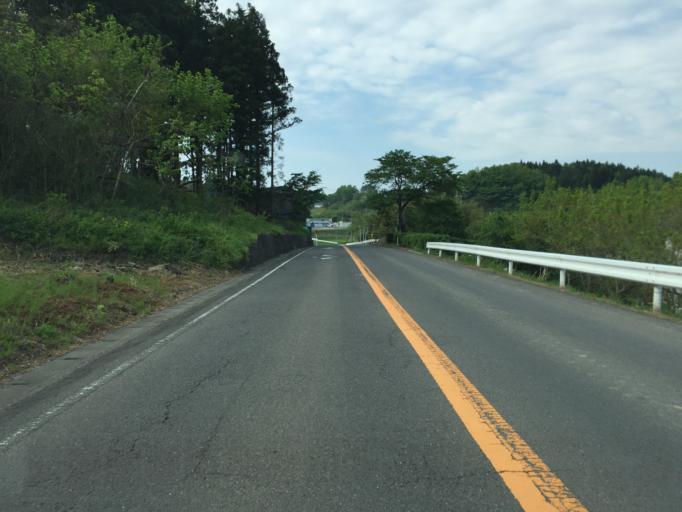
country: JP
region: Fukushima
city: Fukushima-shi
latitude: 37.6721
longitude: 140.5261
